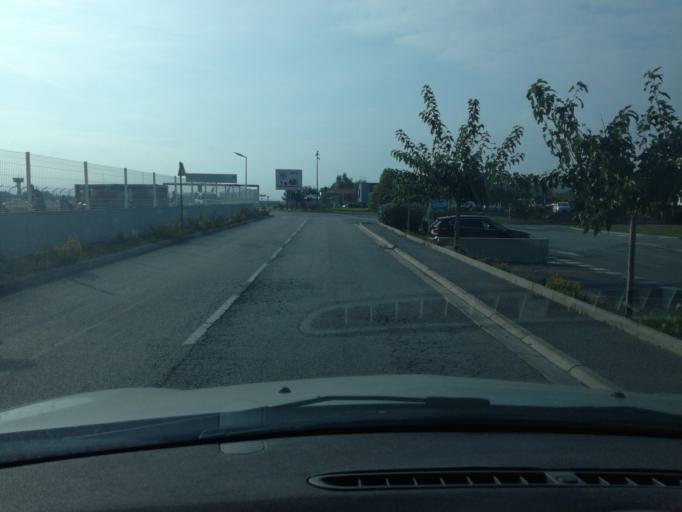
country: FR
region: Provence-Alpes-Cote d'Azur
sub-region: Departement des Alpes-Maritimes
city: Mandelieu-la-Napoule
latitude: 43.5517
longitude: 6.9488
